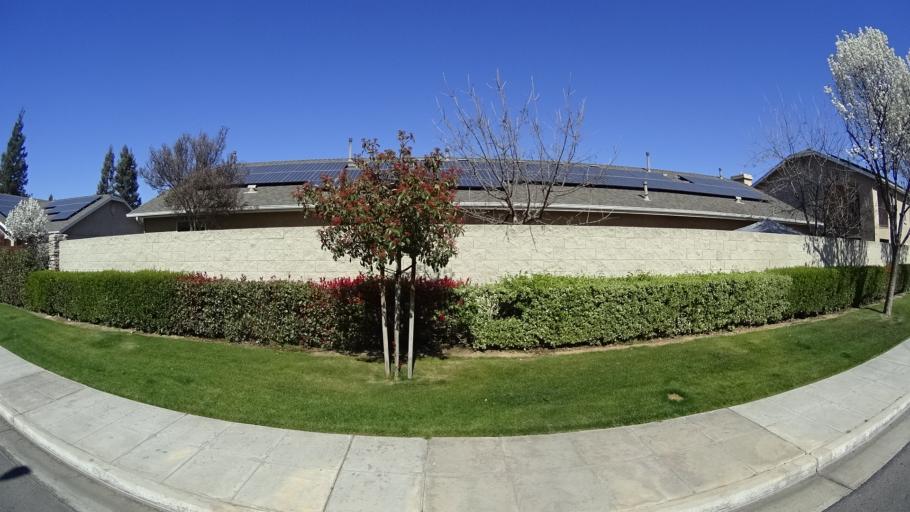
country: US
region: California
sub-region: Fresno County
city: Clovis
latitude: 36.8421
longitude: -119.7495
